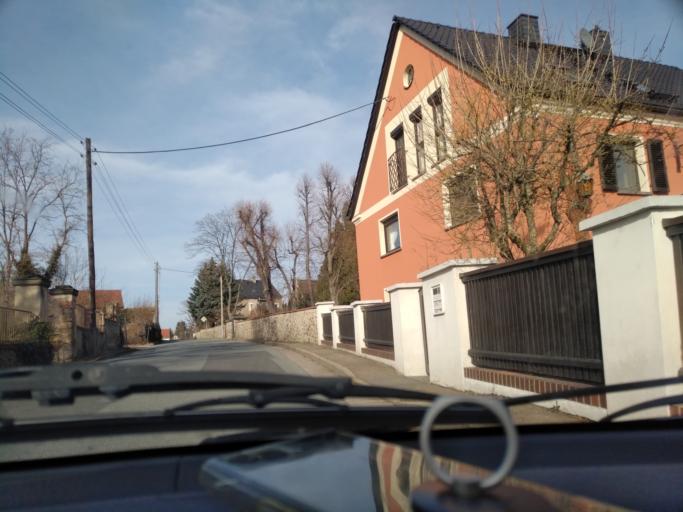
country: DE
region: Saxony
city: Glaubitz
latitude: 51.3190
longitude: 13.3811
